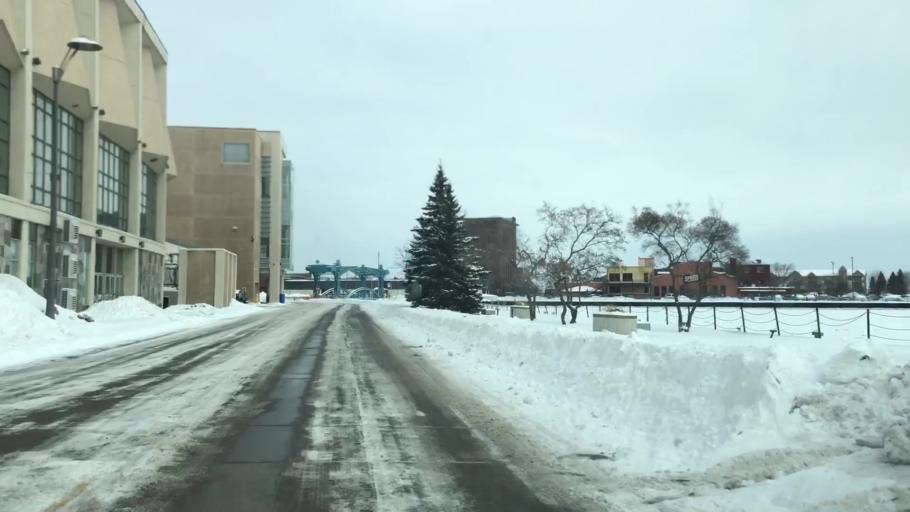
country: US
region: Minnesota
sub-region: Saint Louis County
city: Duluth
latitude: 46.7802
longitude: -92.0979
